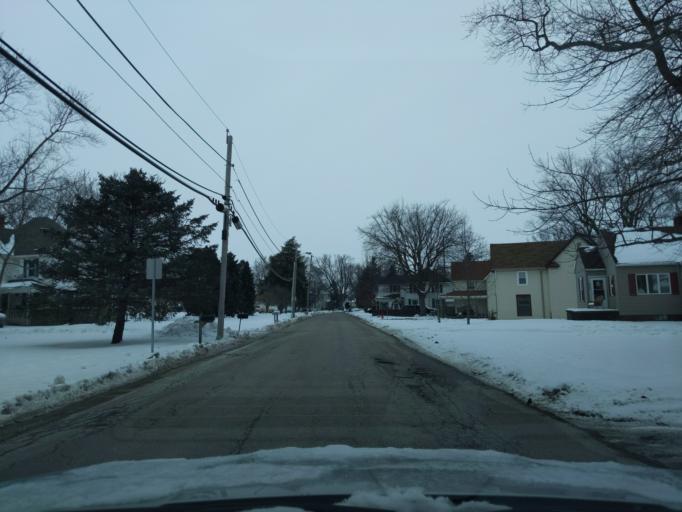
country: US
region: Indiana
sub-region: Benton County
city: Otterbein
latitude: 40.4853
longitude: -87.0956
